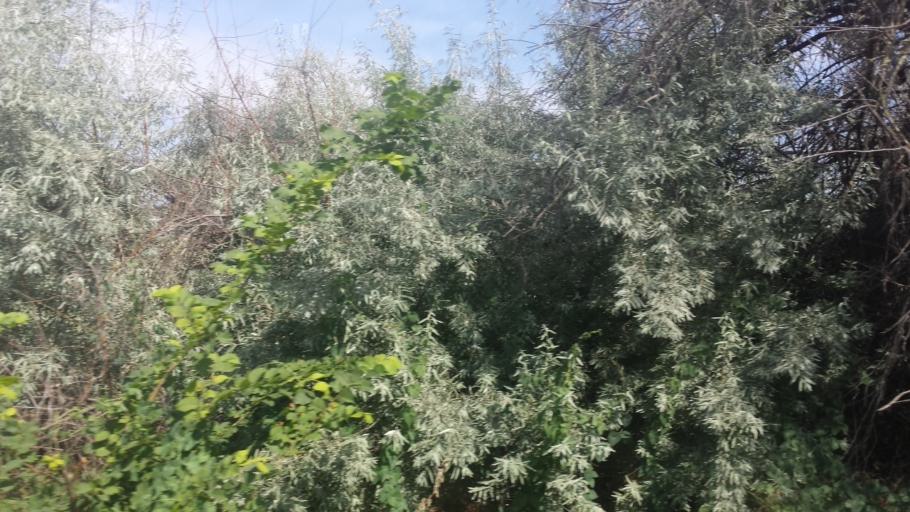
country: RO
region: Constanta
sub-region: Comuna Navodari
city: Navodari
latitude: 44.3240
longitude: 28.6197
